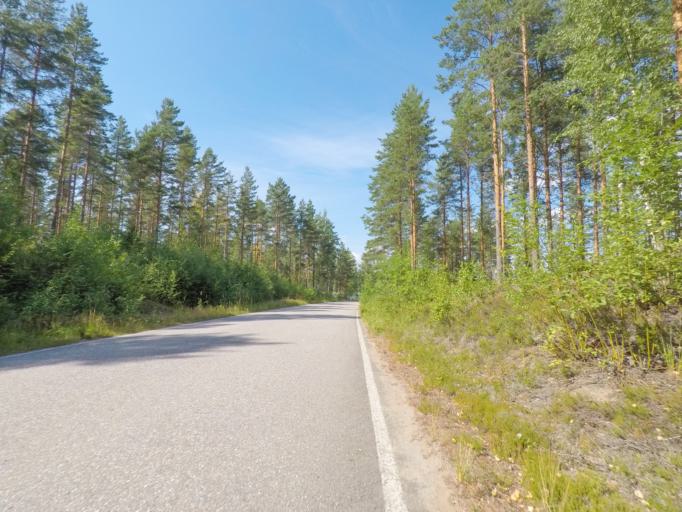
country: FI
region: Southern Savonia
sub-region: Mikkeli
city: Puumala
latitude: 61.4702
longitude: 28.1676
